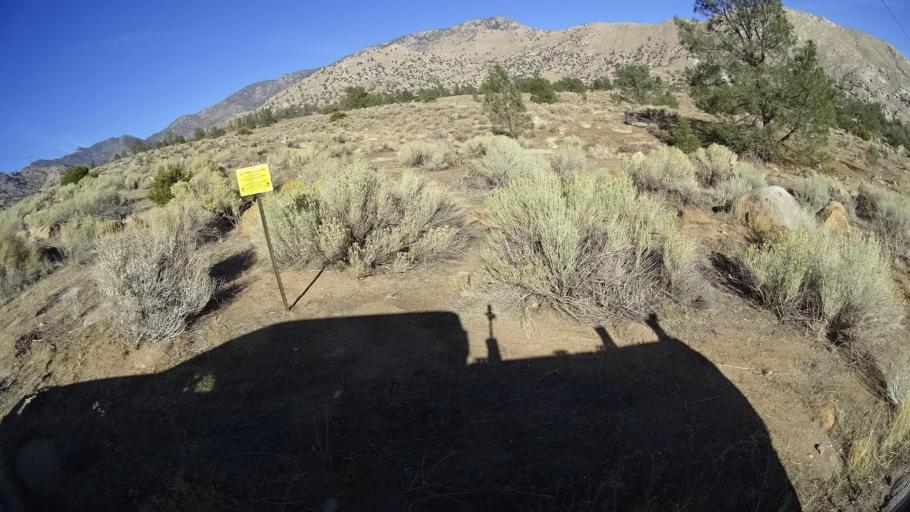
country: US
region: California
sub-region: Kern County
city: Weldon
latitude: 35.6974
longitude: -118.3021
